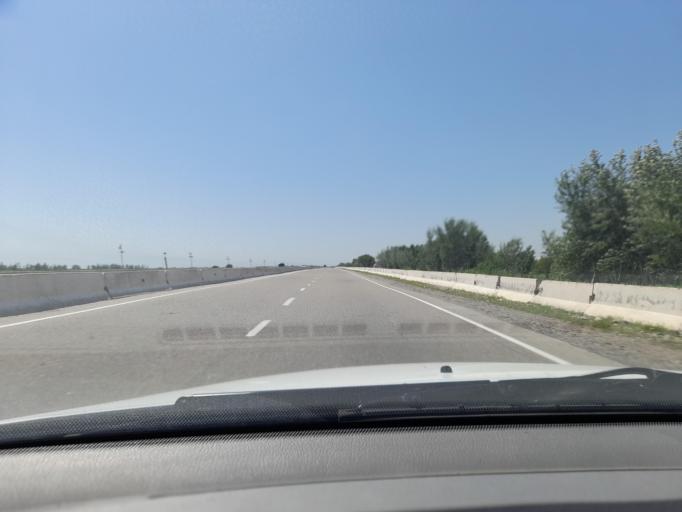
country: UZ
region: Jizzax
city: Paxtakor
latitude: 40.3539
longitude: 68.1347
